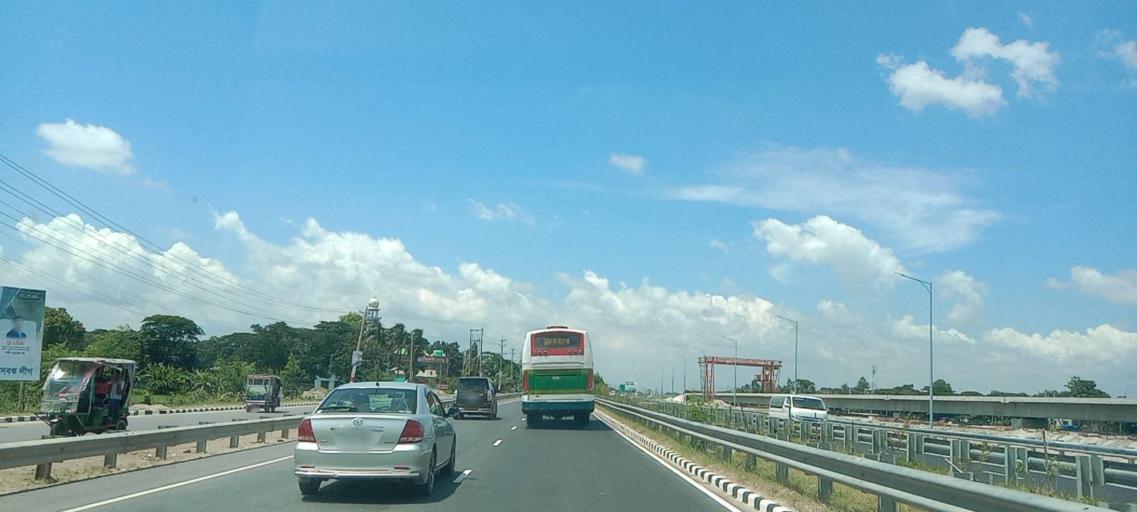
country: BD
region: Dhaka
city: Dohar
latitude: 23.4915
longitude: 90.2692
